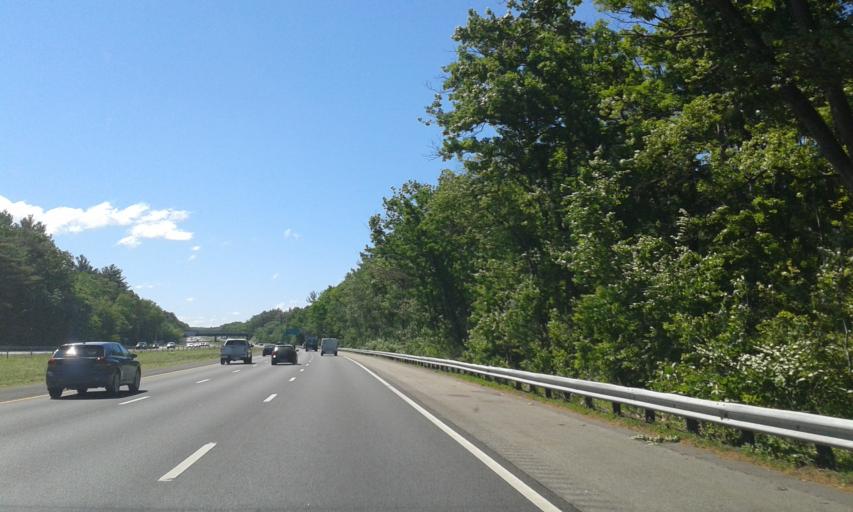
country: US
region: Massachusetts
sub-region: Middlesex County
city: Billerica
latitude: 42.5667
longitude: -71.3021
